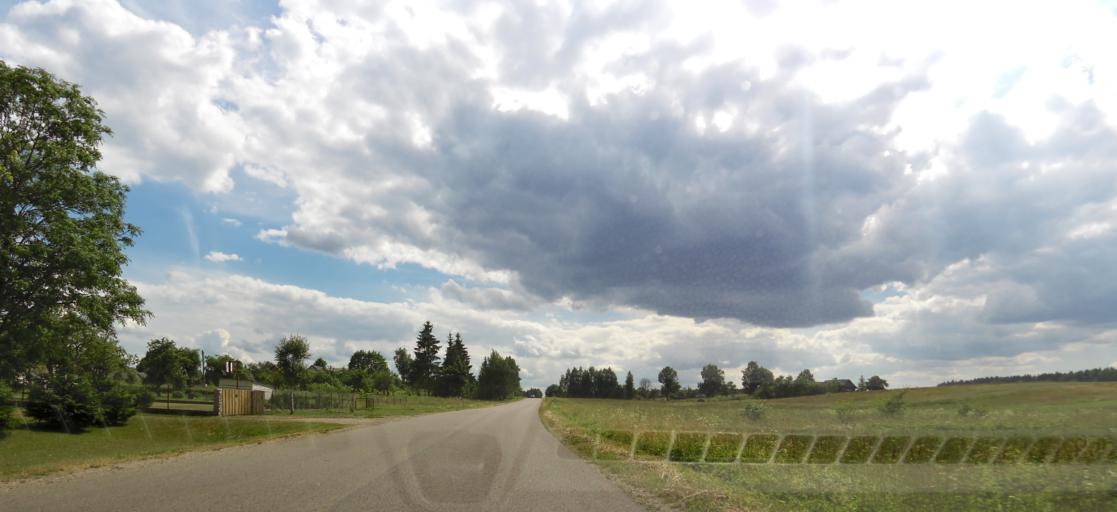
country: LT
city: Skaidiskes
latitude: 54.5357
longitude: 25.6446
